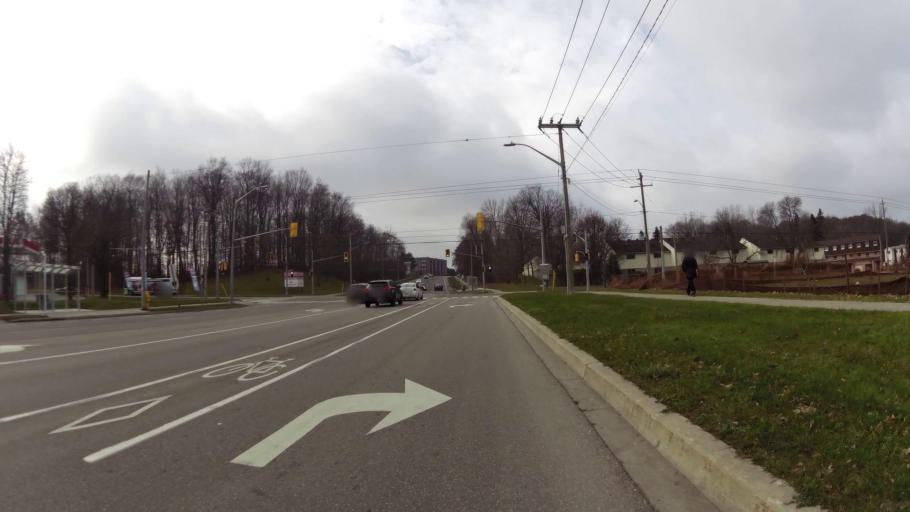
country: CA
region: Ontario
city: Kitchener
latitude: 43.4160
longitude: -80.4793
